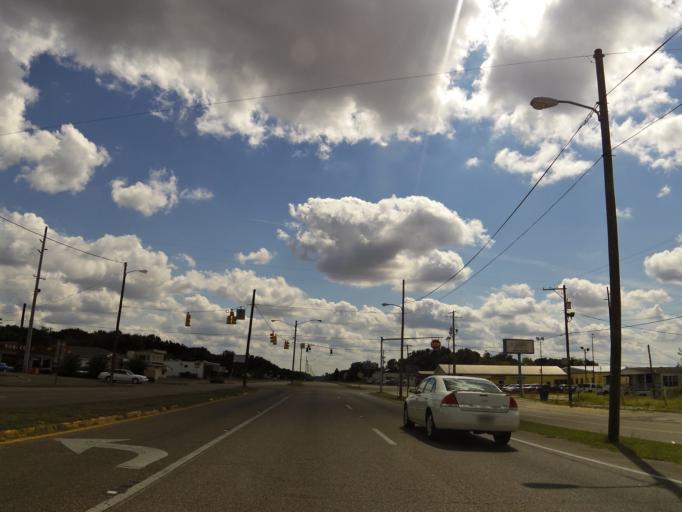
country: US
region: Alabama
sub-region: Dallas County
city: Selma
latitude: 32.4006
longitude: -87.0162
